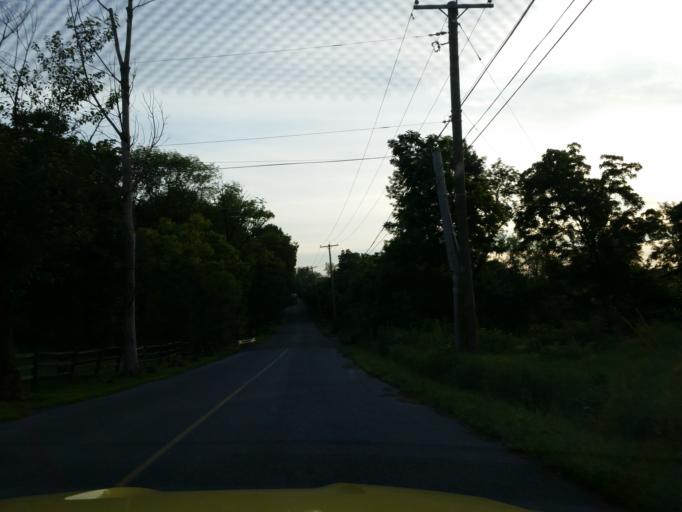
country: US
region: Pennsylvania
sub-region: Lebanon County
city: Fredericksburg
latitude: 40.4473
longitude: -76.3889
